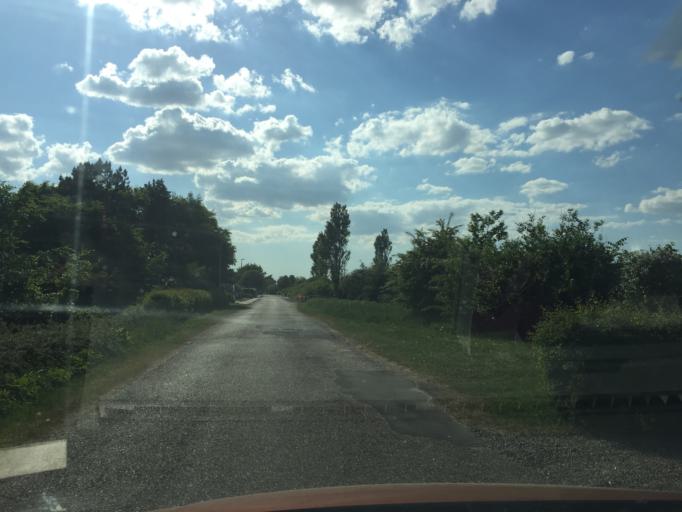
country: DE
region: Schleswig-Holstein
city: Aventoft
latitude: 54.9453
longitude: 8.7992
